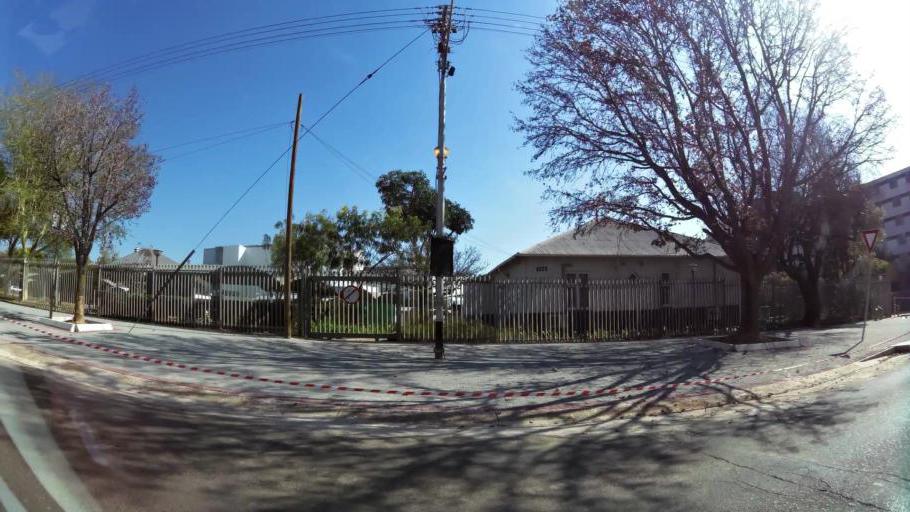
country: ZA
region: Gauteng
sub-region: City of Tshwane Metropolitan Municipality
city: Pretoria
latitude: -25.7540
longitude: 28.2354
